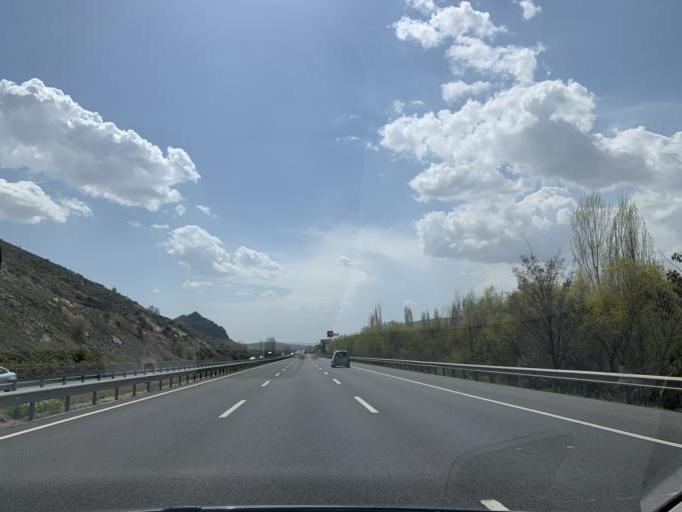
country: TR
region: Ankara
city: Temelli
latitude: 39.7818
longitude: 32.5096
